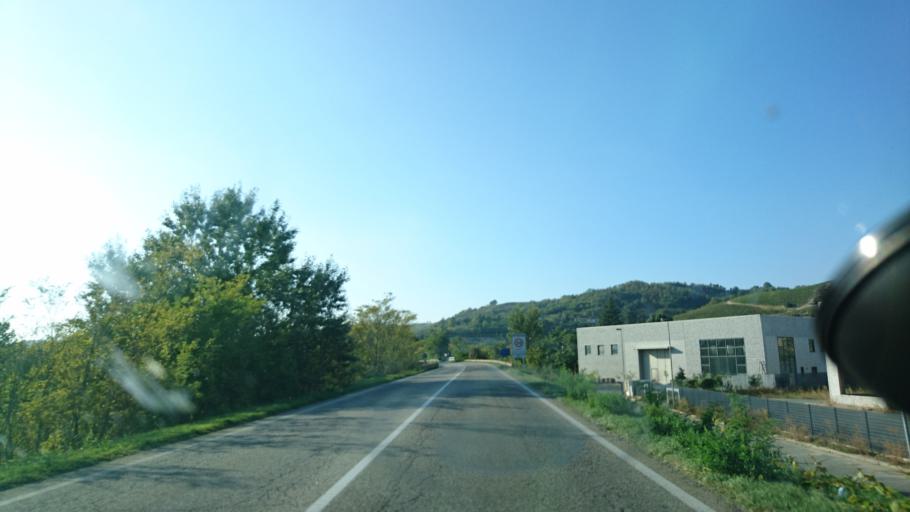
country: IT
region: Piedmont
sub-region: Provincia di Alessandria
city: Terzo
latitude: 44.6741
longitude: 8.4412
